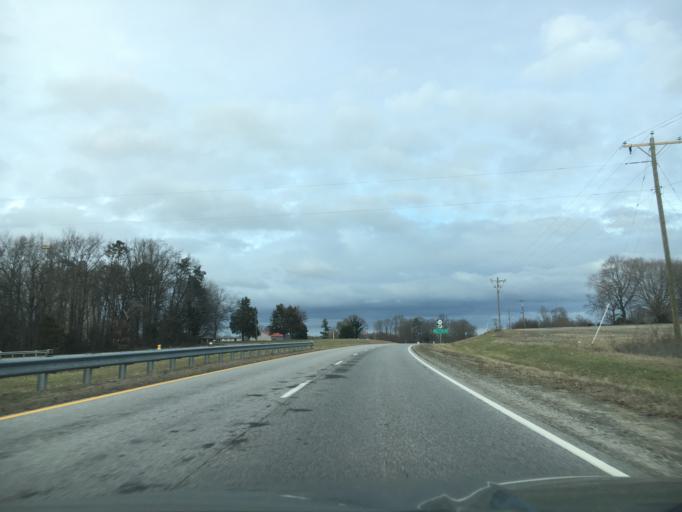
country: US
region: Virginia
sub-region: Nottoway County
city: Crewe
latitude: 37.2623
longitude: -78.1363
